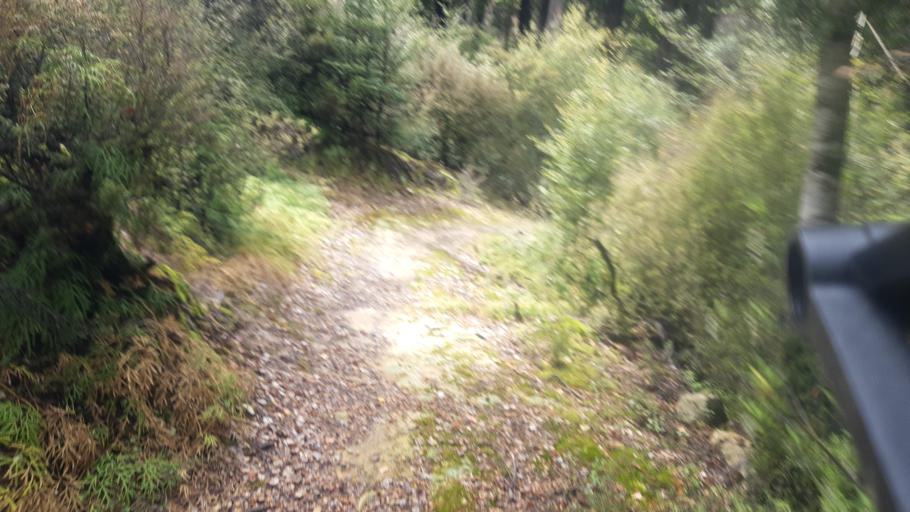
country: NZ
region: Tasman
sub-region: Tasman District
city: Wakefield
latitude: -41.7600
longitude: 172.8039
